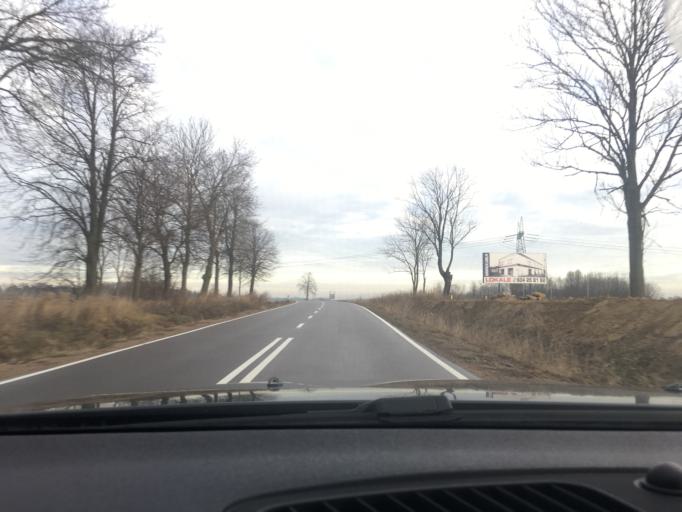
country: PL
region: Swietokrzyskie
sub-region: Powiat jedrzejowski
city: Jedrzejow
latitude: 50.6542
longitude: 20.3231
